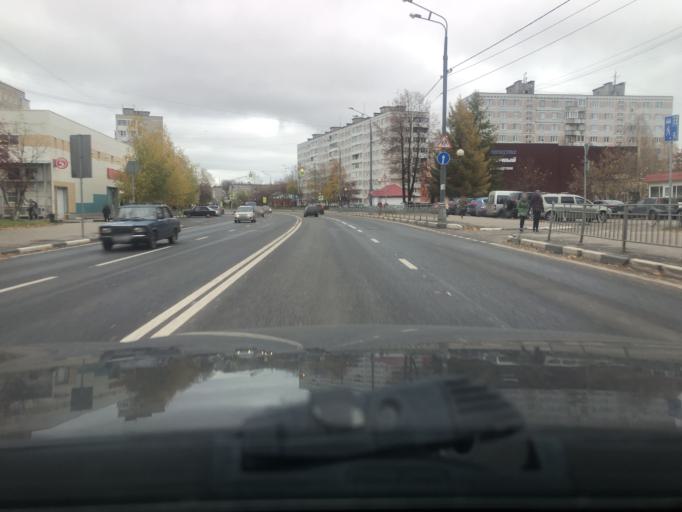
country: RU
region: Moskovskaya
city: Sergiyev Posad
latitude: 56.3238
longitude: 38.1347
